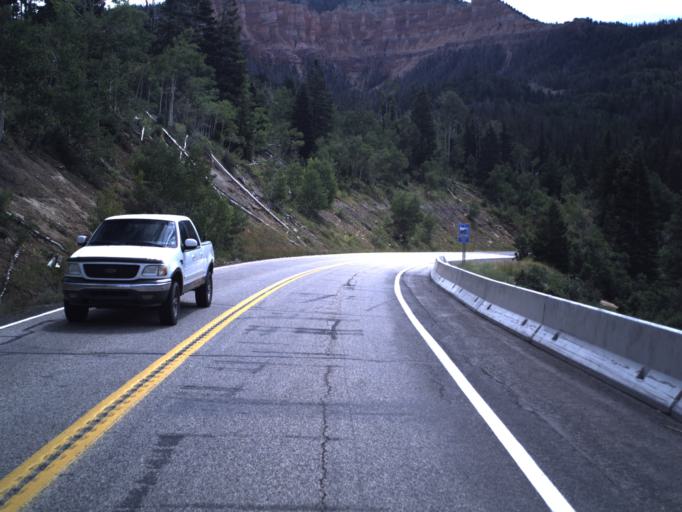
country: US
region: Utah
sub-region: Iron County
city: Cedar City
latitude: 37.5921
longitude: -112.8994
